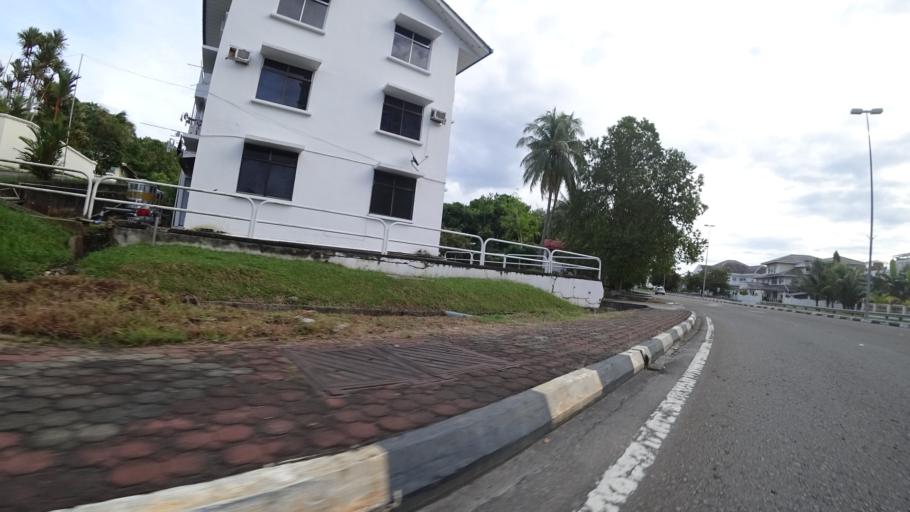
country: BN
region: Brunei and Muara
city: Bandar Seri Begawan
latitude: 4.9040
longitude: 114.9398
